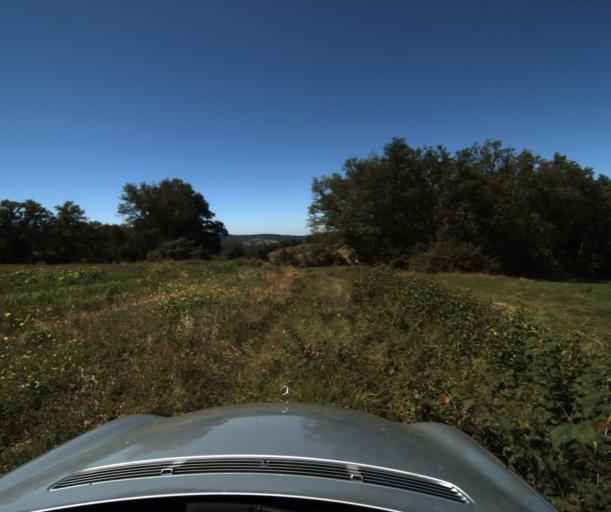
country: FR
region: Midi-Pyrenees
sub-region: Departement de l'Ariege
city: Belesta
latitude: 42.9642
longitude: 1.9238
